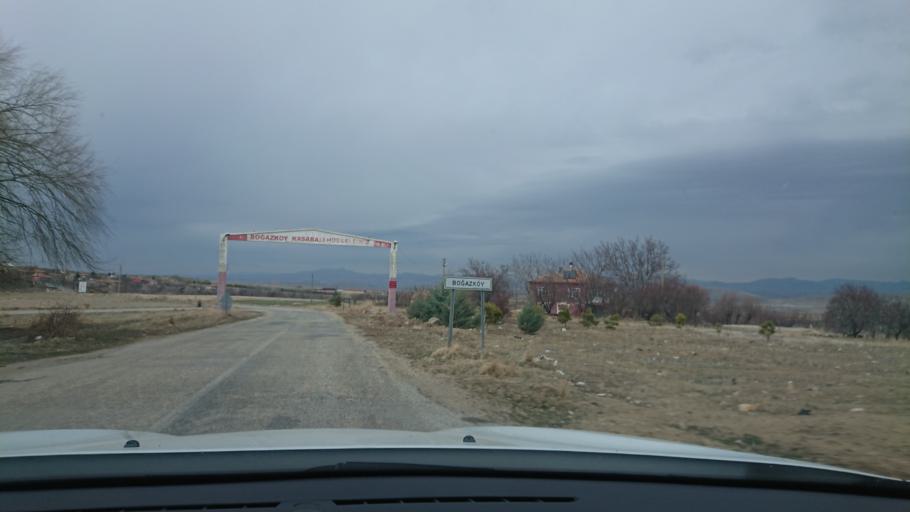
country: TR
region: Aksaray
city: Sariyahsi
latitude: 38.9572
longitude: 33.8944
